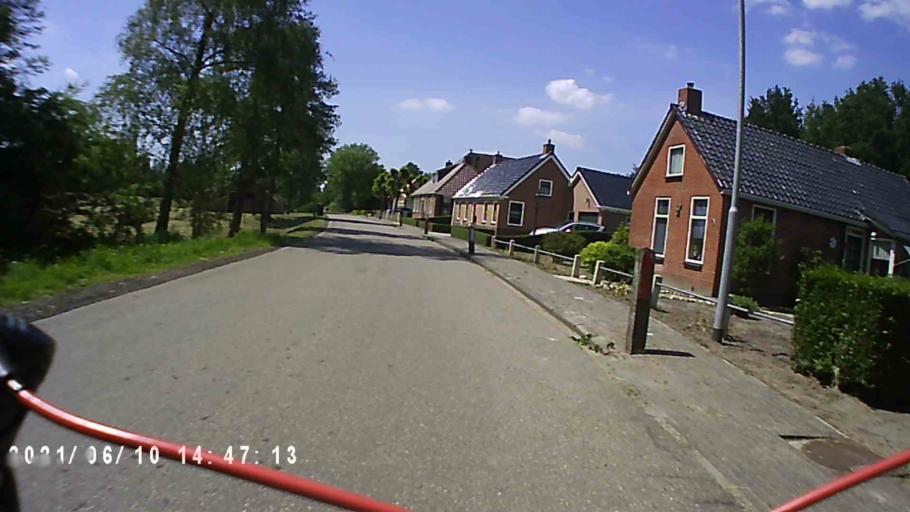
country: NL
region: Groningen
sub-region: Gemeente Grootegast
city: Grootegast
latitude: 53.2362
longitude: 6.2674
